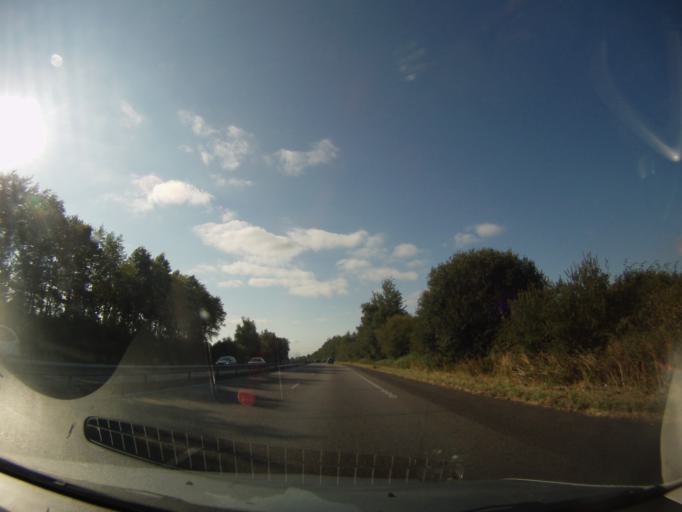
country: FR
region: Pays de la Loire
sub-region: Departement de la Loire-Atlantique
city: Orvault
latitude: 47.2865
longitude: -1.6064
